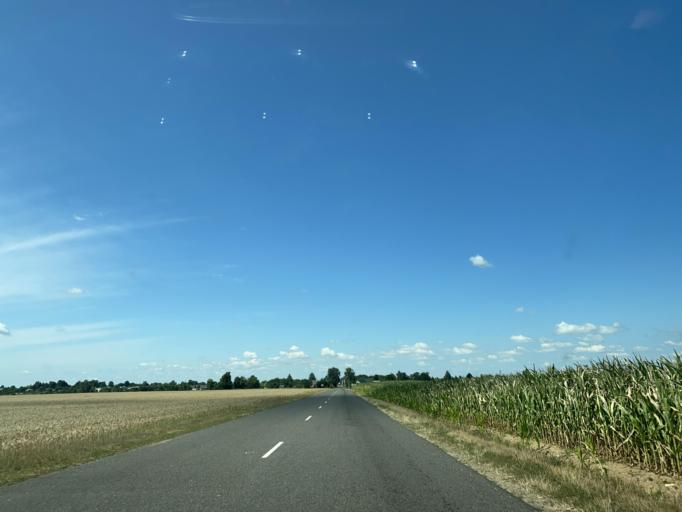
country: BY
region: Brest
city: Ivanava
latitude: 52.1735
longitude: 25.5687
